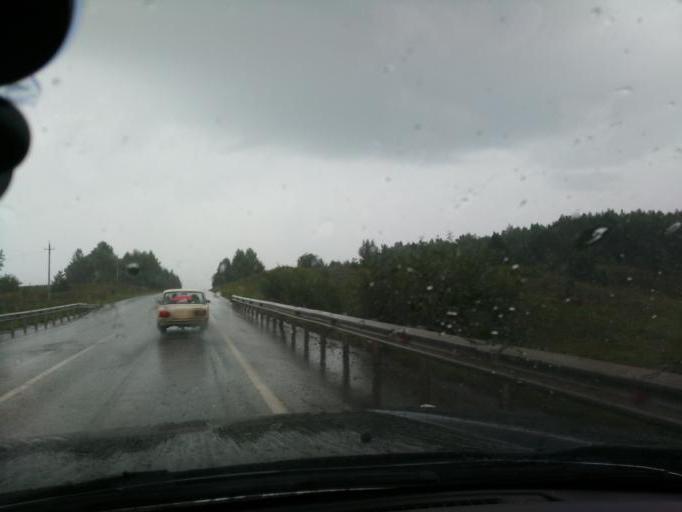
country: RU
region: Perm
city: Osa
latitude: 57.1496
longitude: 55.5293
